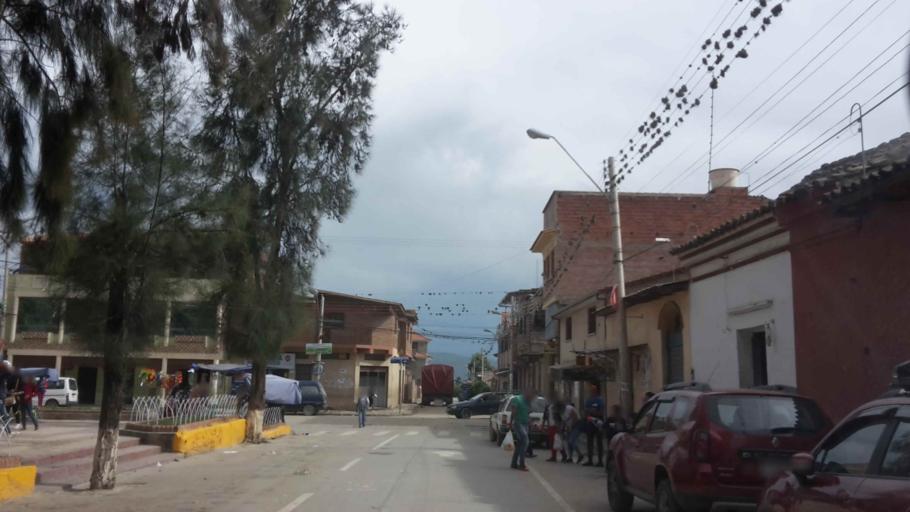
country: BO
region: Cochabamba
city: Cochabamba
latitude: -17.3381
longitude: -66.2660
